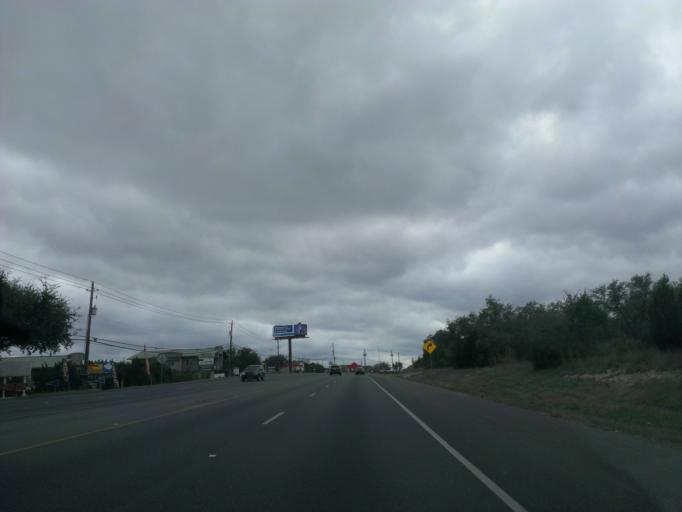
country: US
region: Texas
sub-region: Travis County
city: Hudson Bend
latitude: 30.3845
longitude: -97.9429
